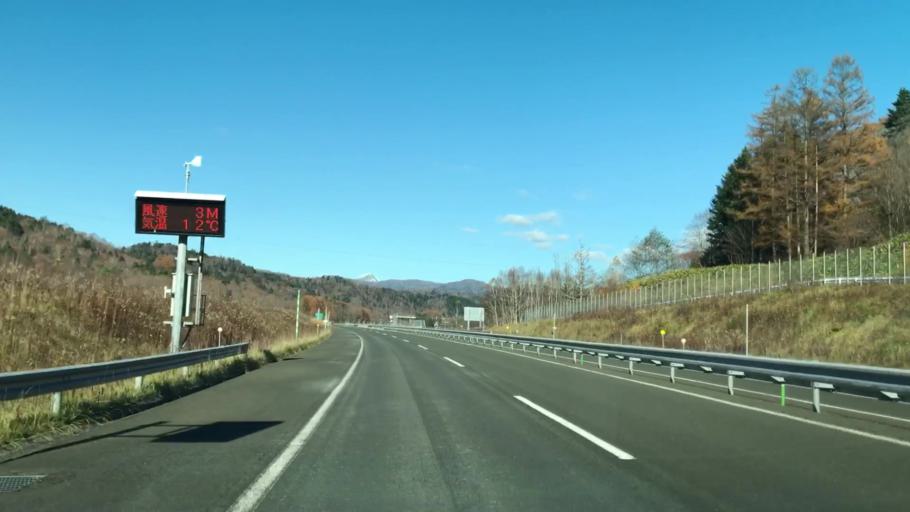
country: JP
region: Hokkaido
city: Shimo-furano
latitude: 42.9262
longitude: 142.2034
